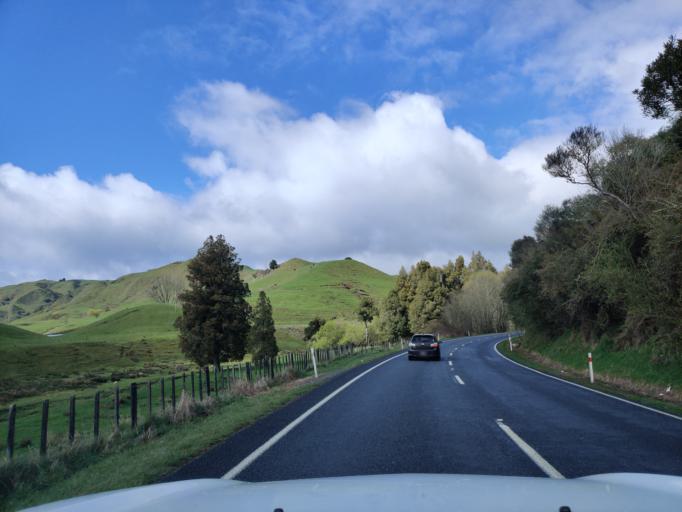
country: NZ
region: Waikato
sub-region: Otorohanga District
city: Otorohanga
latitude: -38.5935
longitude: 175.2196
